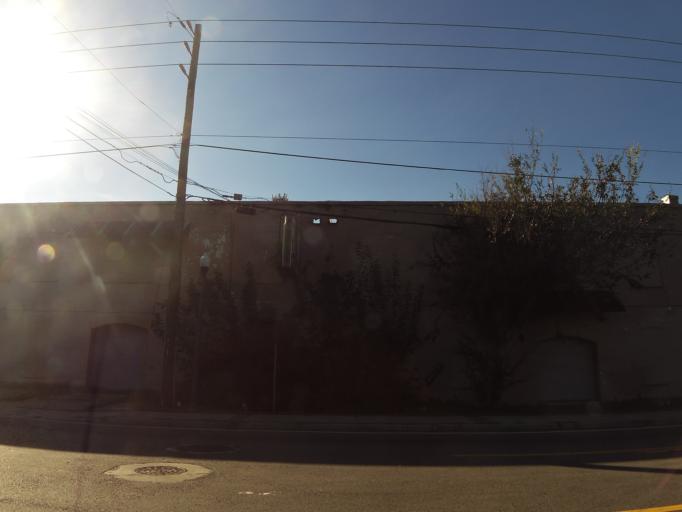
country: US
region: Florida
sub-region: Duval County
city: Jacksonville
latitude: 30.3544
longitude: -81.6759
